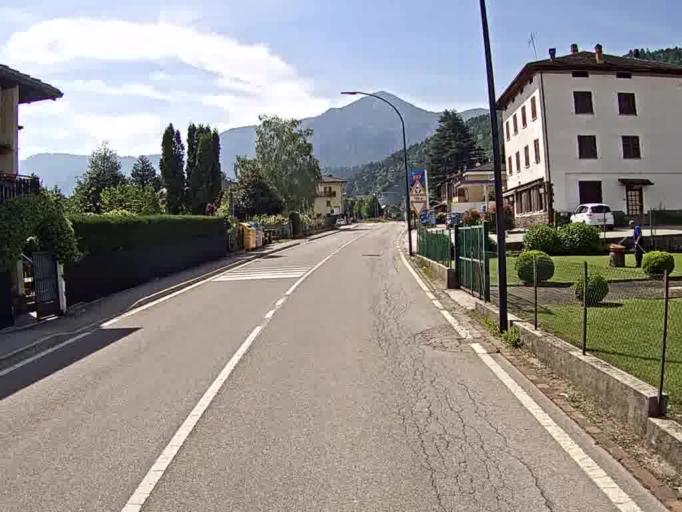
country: IT
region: Trentino-Alto Adige
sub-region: Provincia di Trento
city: Calceranica al Lago
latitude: 46.0065
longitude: 11.2410
